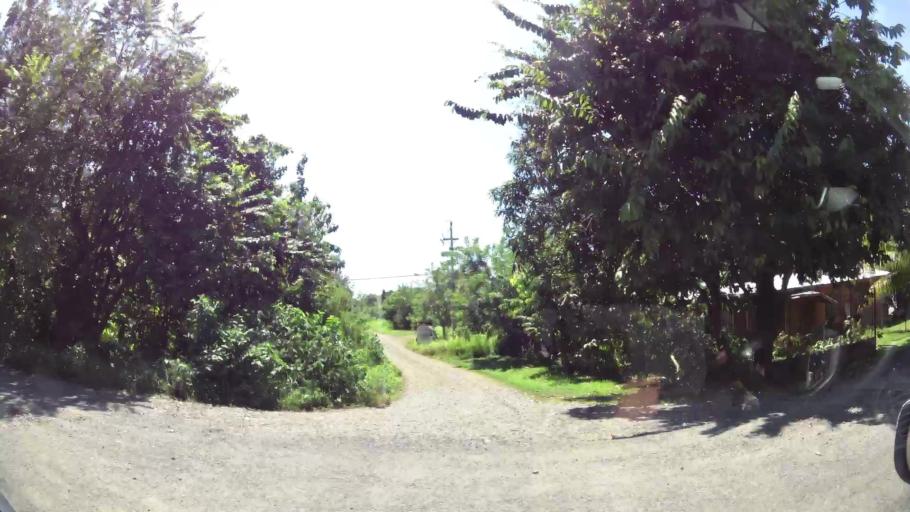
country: CR
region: Puntarenas
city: Quepos
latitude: 9.3295
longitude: -83.9549
